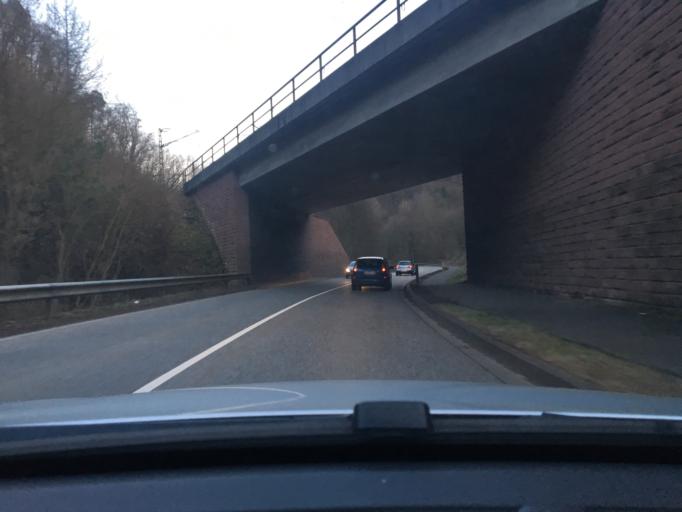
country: DE
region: Rheinland-Pfalz
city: Neidenfels
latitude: 49.3922
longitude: 8.0385
